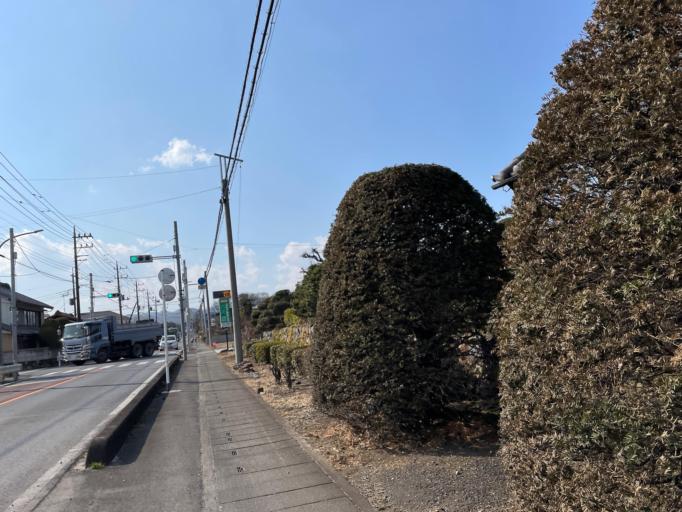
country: JP
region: Saitama
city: Yorii
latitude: 36.1259
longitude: 139.2259
